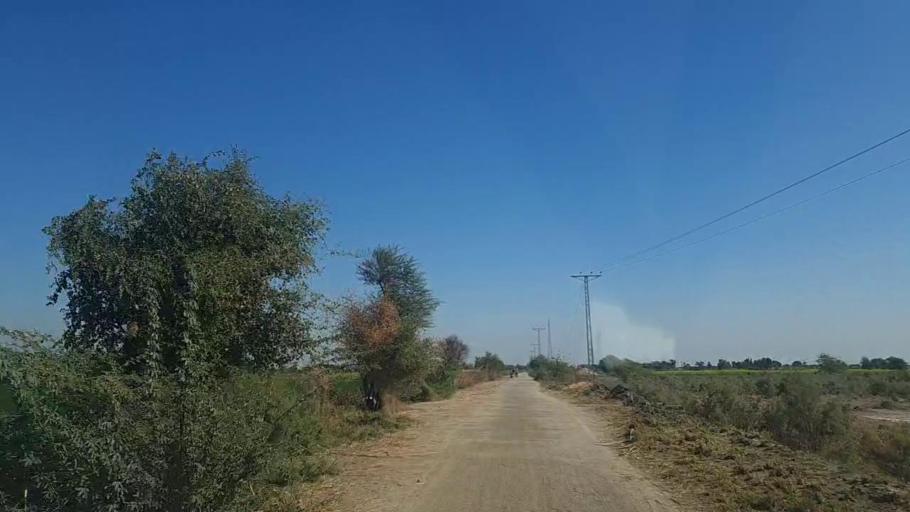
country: PK
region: Sindh
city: Khadro
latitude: 26.1773
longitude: 68.8203
